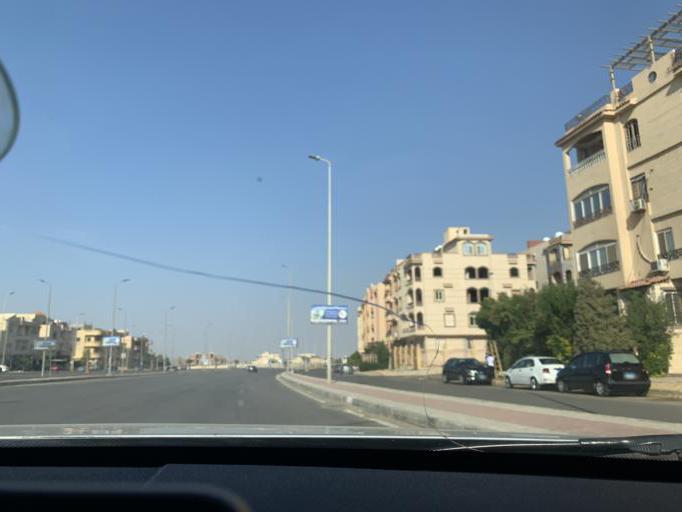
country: EG
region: Muhafazat al Qahirah
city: Cairo
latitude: 30.0045
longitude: 31.4692
